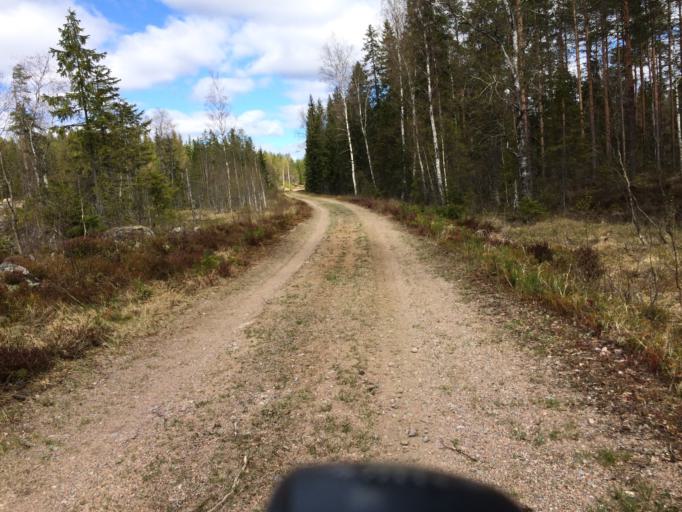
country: SE
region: OErebro
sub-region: Hallefors Kommun
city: Haellefors
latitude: 60.0543
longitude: 14.5235
